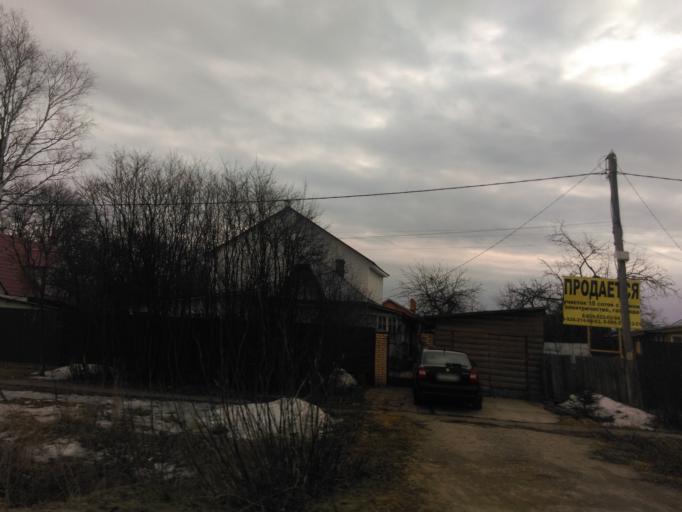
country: RU
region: Moskovskaya
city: Zvenigorod
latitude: 55.7352
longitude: 36.9339
